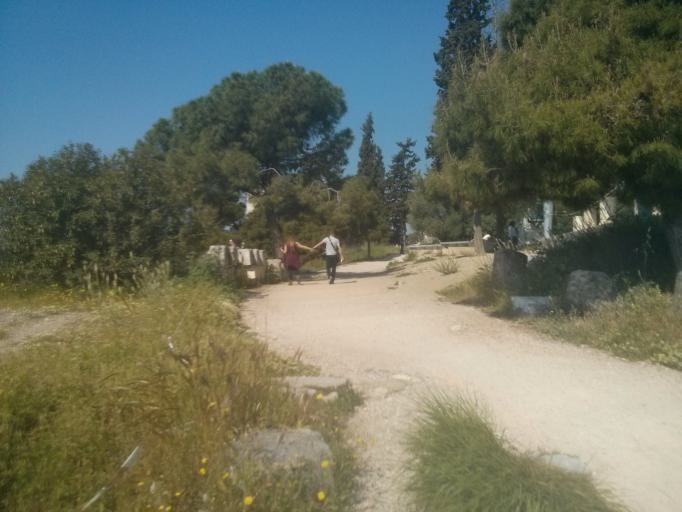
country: GR
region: Attica
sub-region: Nomarchia Athinas
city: Athens
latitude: 37.9708
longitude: 23.7261
